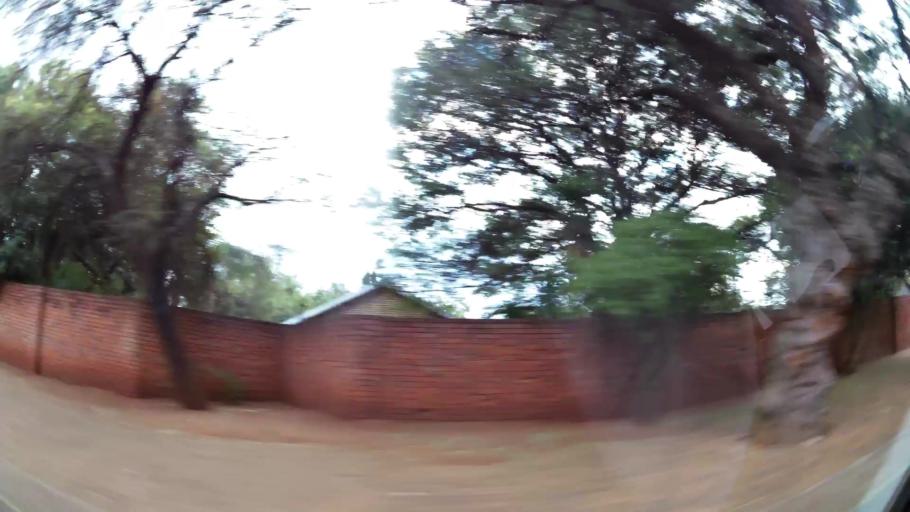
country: ZA
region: Limpopo
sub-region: Waterberg District Municipality
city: Mokopane
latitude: -24.2007
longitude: 29.0046
